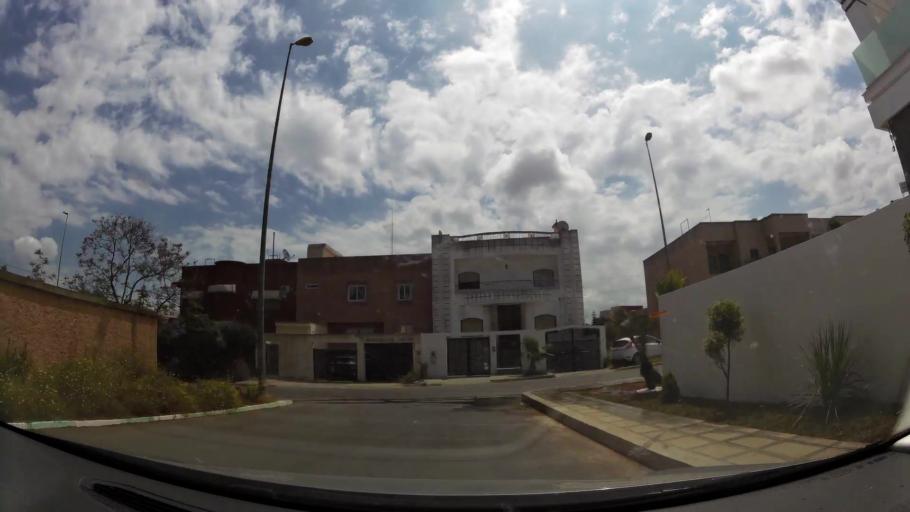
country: MA
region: Gharb-Chrarda-Beni Hssen
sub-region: Kenitra Province
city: Kenitra
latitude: 34.2439
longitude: -6.6076
